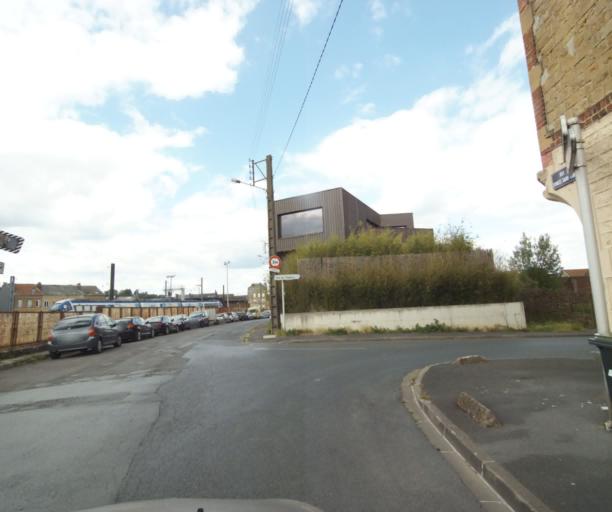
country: FR
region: Champagne-Ardenne
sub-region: Departement des Ardennes
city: Charleville-Mezieres
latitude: 49.7697
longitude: 4.7281
